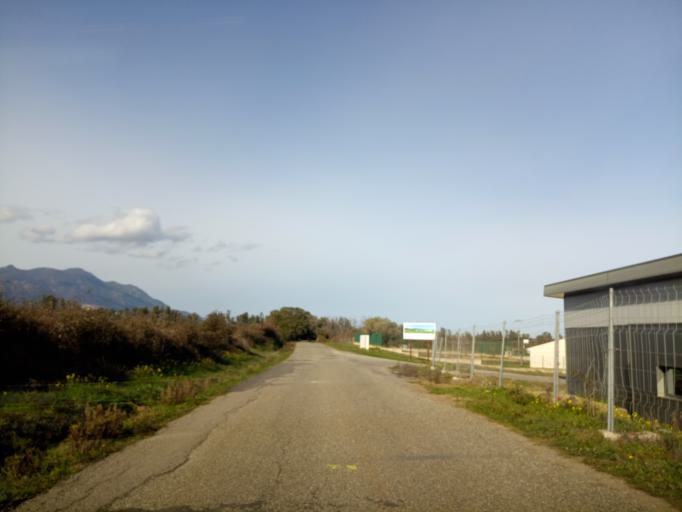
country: FR
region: Corsica
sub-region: Departement de la Haute-Corse
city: Linguizzetta
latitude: 42.2621
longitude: 9.5445
